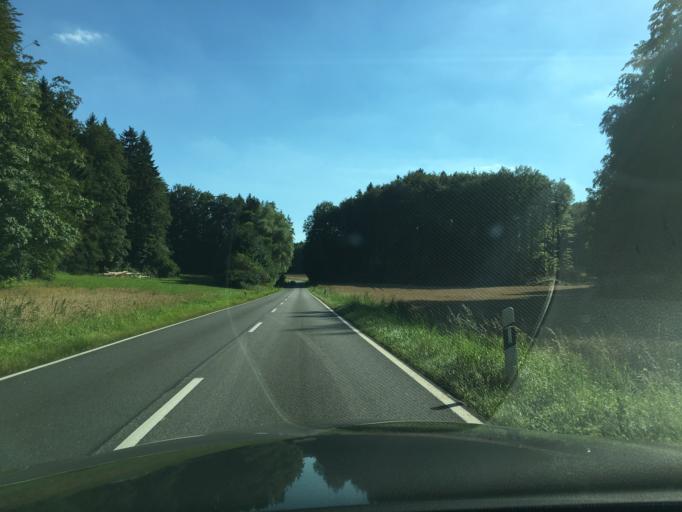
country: DE
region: Bavaria
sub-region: Upper Franconia
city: Hiltpoltstein
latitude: 49.6684
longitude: 11.3481
